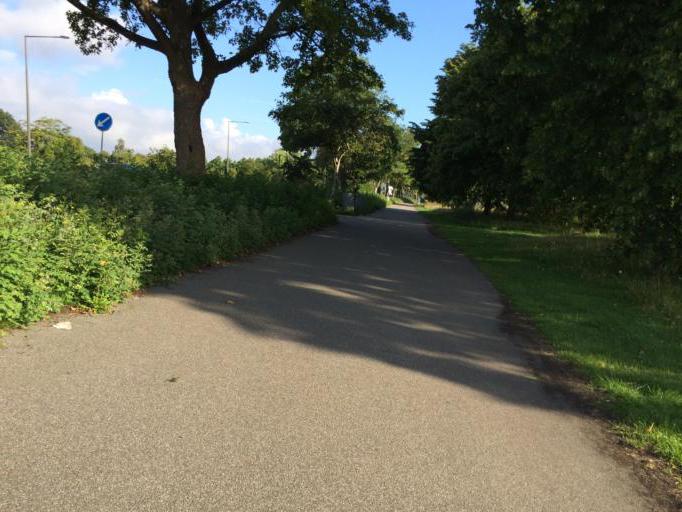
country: DK
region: Capital Region
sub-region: Tarnby Kommune
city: Tarnby
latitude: 55.6487
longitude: 12.6418
